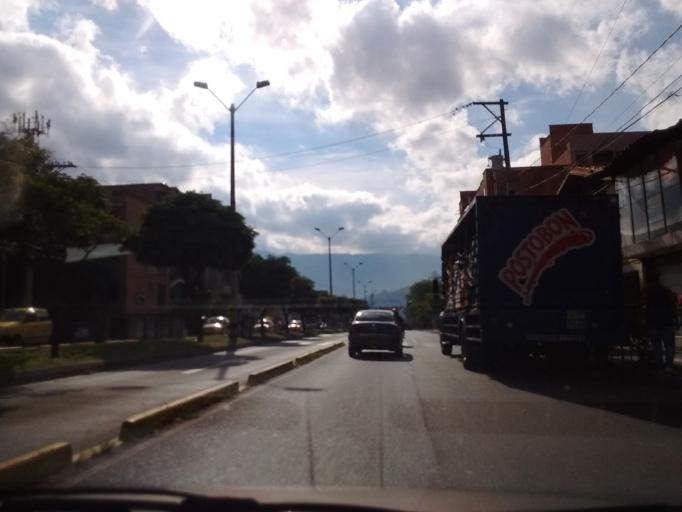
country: CO
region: Antioquia
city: Medellin
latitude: 6.2314
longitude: -75.5931
